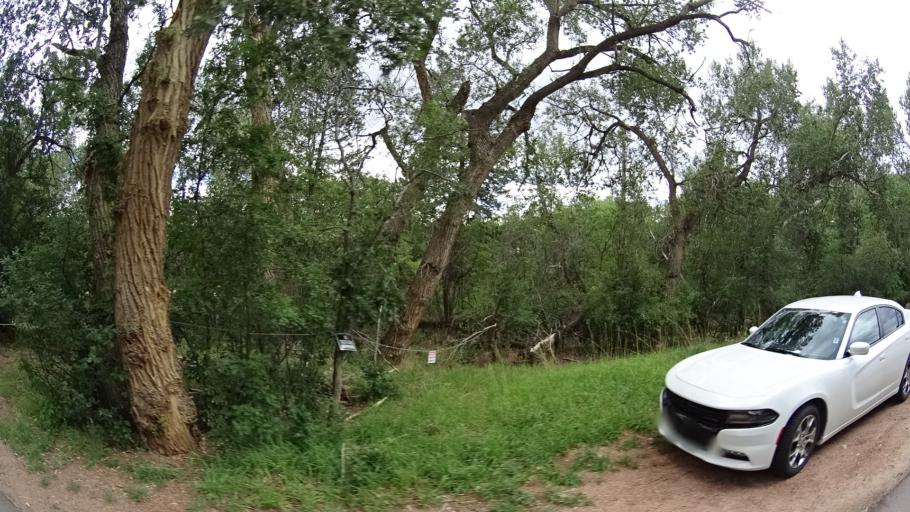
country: US
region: Colorado
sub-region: El Paso County
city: Manitou Springs
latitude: 38.8438
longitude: -104.9025
